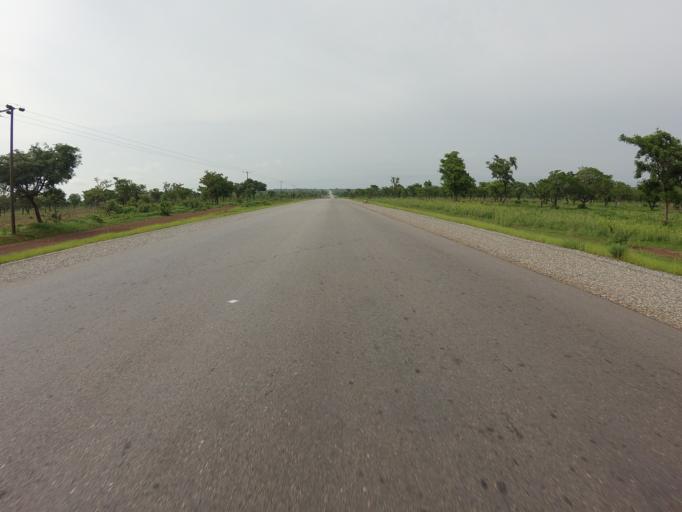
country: GH
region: Northern
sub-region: Yendi
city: Yendi
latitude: 9.6352
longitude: -0.0616
